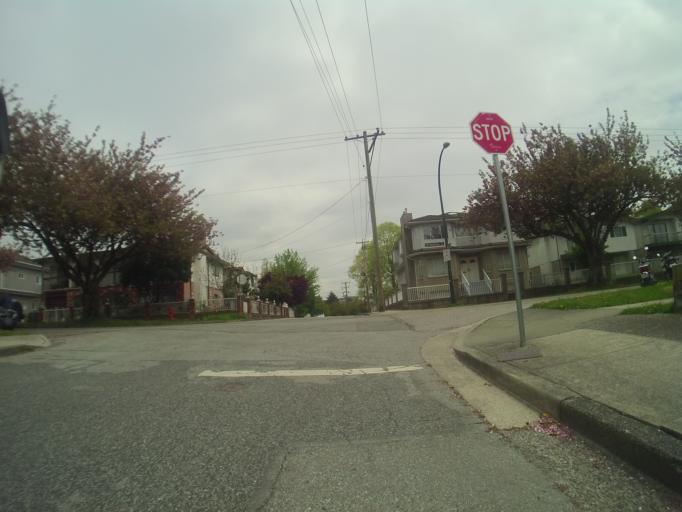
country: CA
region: British Columbia
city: Vancouver
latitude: 49.2430
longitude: -123.0738
